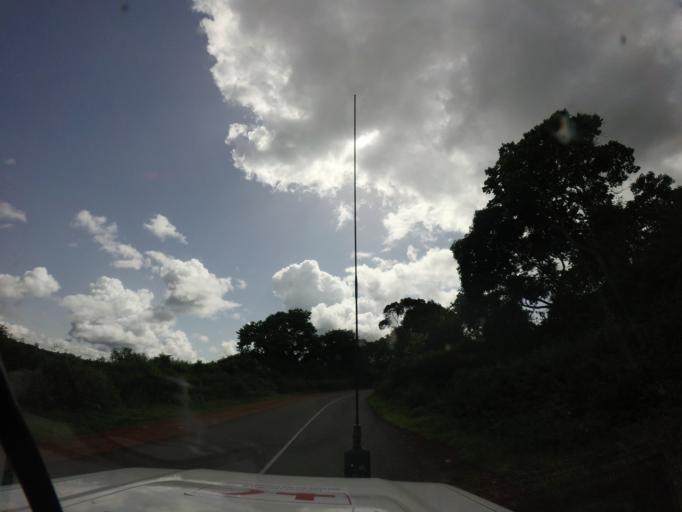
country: GN
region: Mamou
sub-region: Mamou Prefecture
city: Mamou
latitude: 10.3480
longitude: -12.0456
